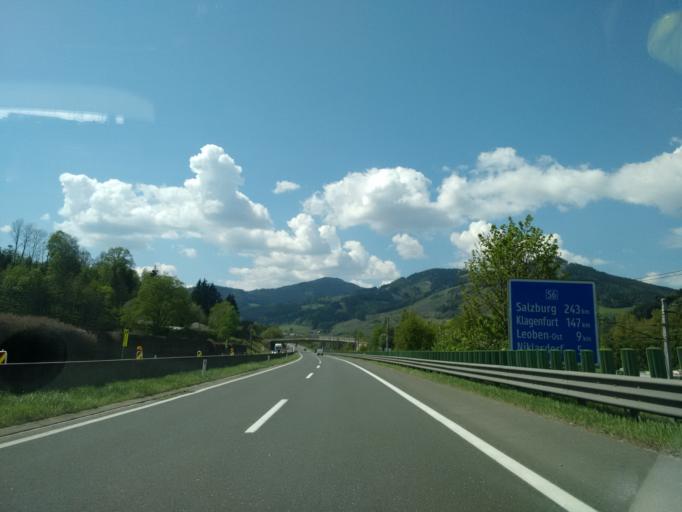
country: AT
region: Styria
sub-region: Politischer Bezirk Bruck-Muerzzuschlag
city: Oberaich
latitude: 47.4039
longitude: 15.2200
